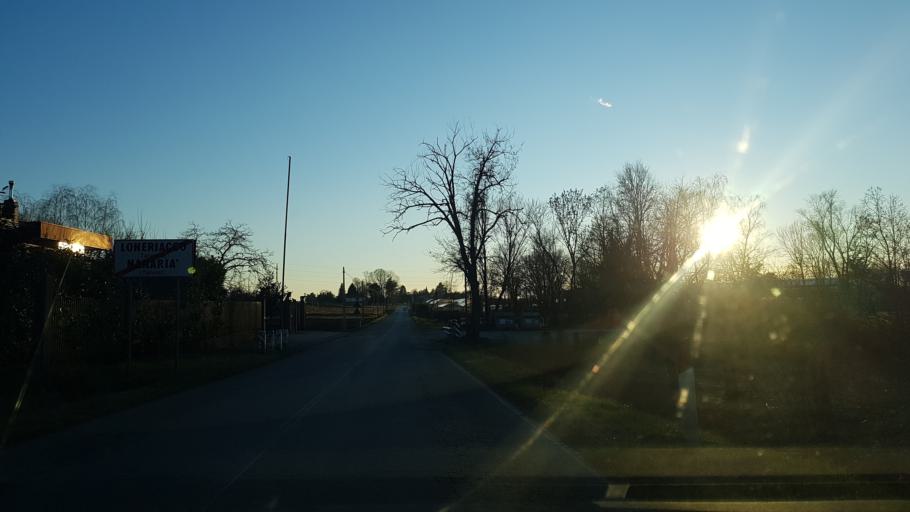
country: IT
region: Friuli Venezia Giulia
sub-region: Provincia di Udine
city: Tarcento
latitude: 46.1908
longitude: 13.2256
